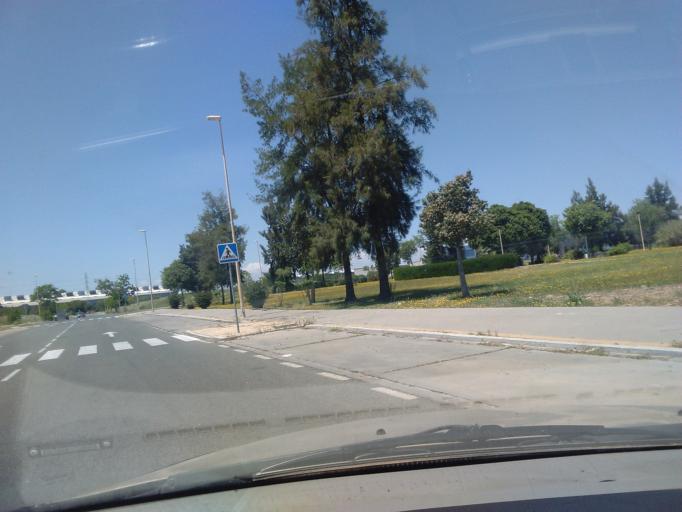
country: ES
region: Andalusia
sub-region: Provincia de Sevilla
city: Sevilla
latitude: 37.3783
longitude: -5.9296
